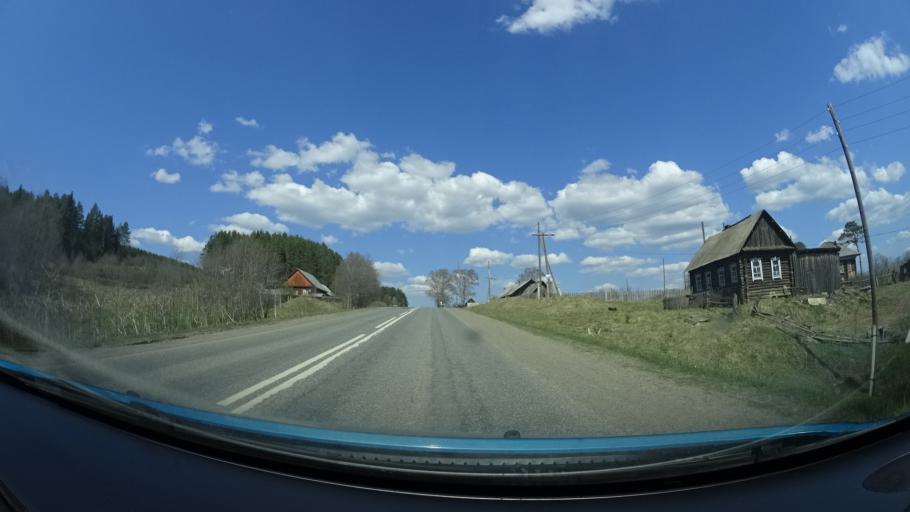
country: RU
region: Perm
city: Yugo-Kamskiy
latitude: 57.5480
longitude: 55.6845
